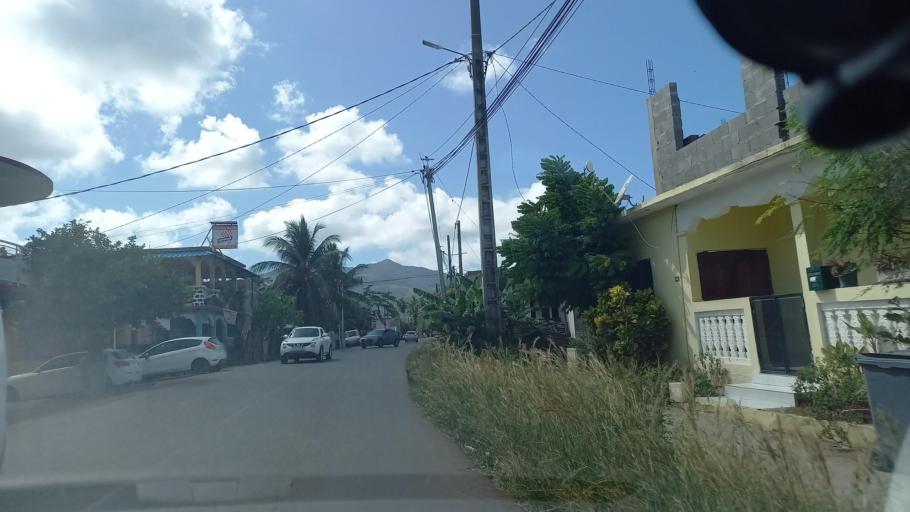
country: YT
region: Chirongui
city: Chirongui
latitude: -12.9291
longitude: 45.1531
